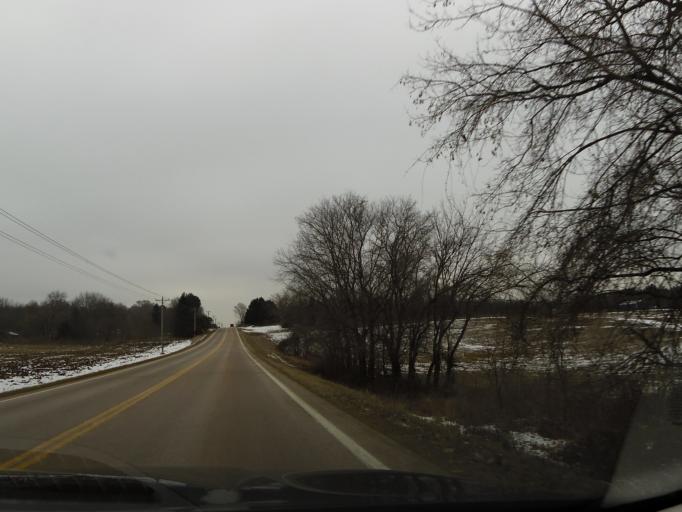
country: US
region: Minnesota
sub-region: Carver County
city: Carver
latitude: 44.7181
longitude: -93.6559
